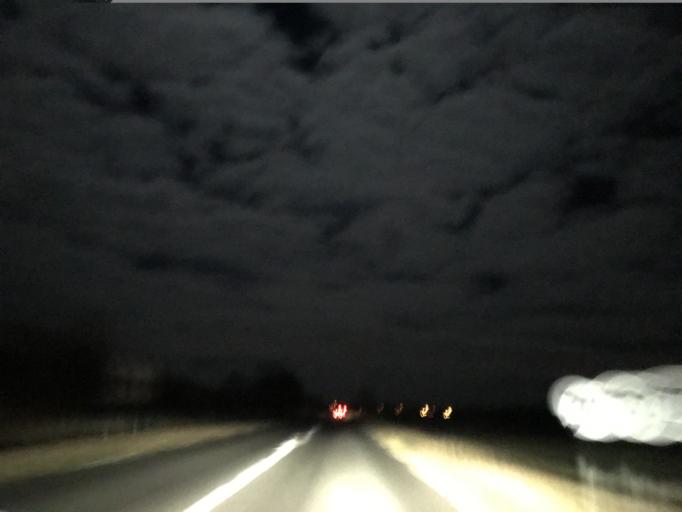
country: FR
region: Auvergne
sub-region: Departement de l'Allier
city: Hauterive
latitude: 46.0877
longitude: 3.4424
